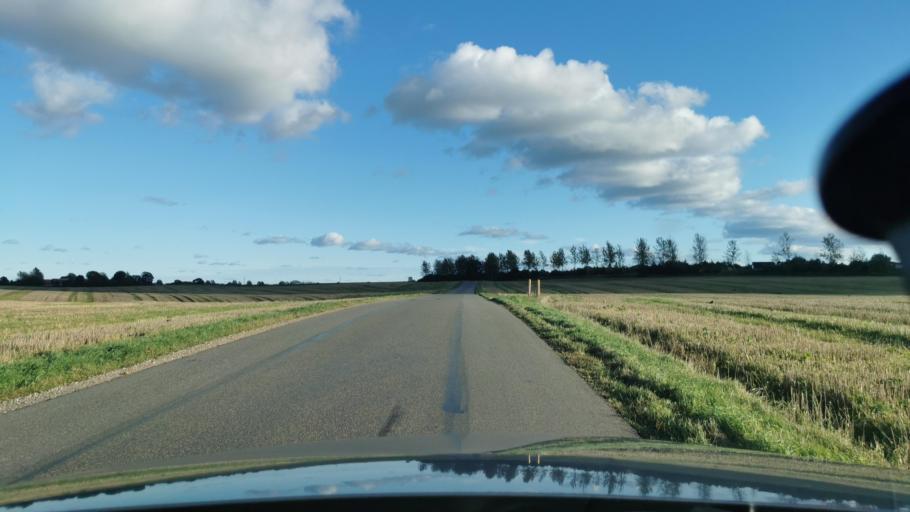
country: DK
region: Capital Region
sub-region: Hoje-Taastrup Kommune
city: Flong
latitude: 55.6659
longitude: 12.1472
